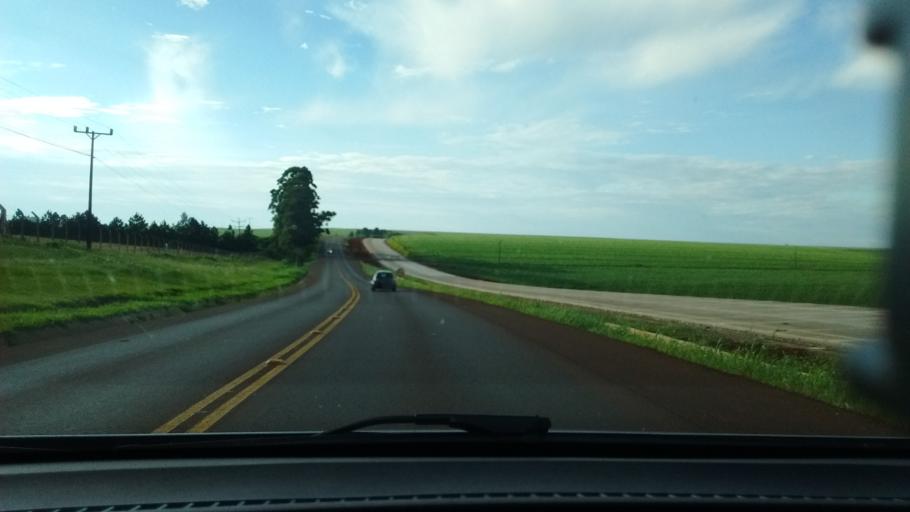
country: BR
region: Parana
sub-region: Cascavel
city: Cascavel
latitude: -25.0984
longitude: -53.5938
